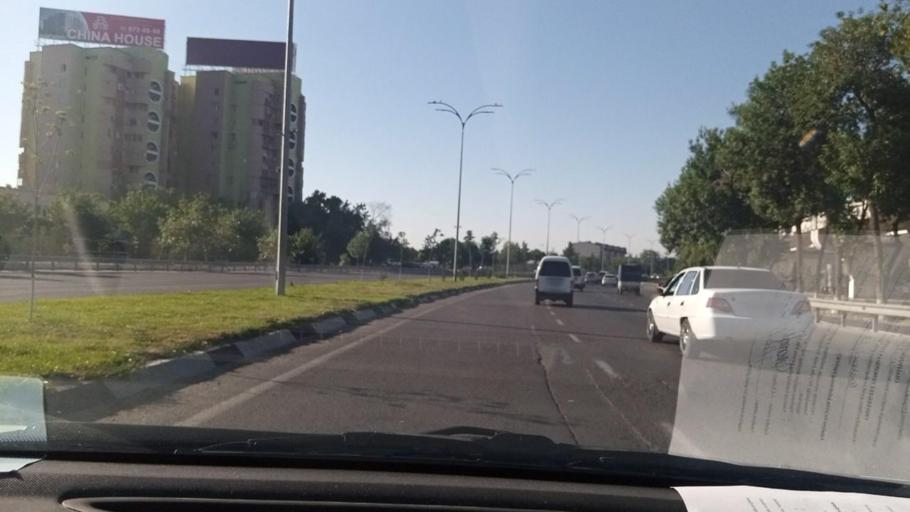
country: UZ
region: Toshkent Shahri
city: Bektemir
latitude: 41.2898
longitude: 69.3588
